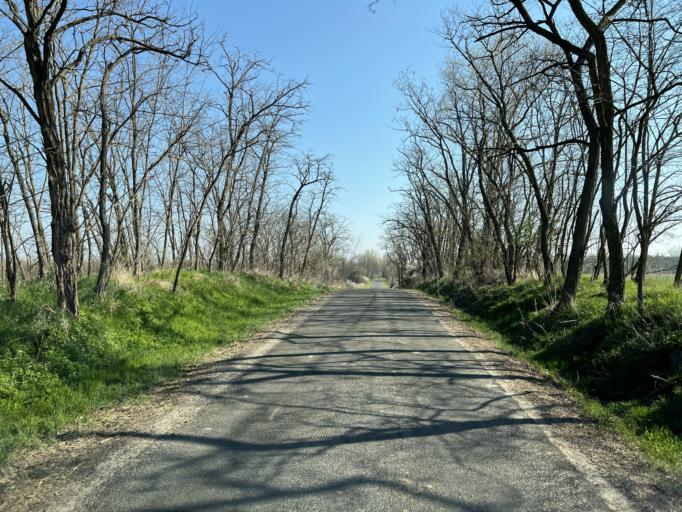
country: SK
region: Nitriansky
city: Sahy
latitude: 48.0294
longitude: 18.8317
